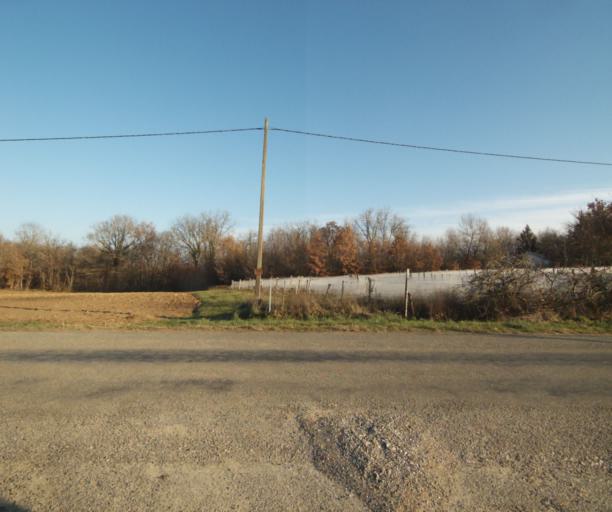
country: FR
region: Midi-Pyrenees
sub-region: Departement du Tarn-et-Garonne
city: Moissac
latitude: 44.1440
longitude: 1.1222
